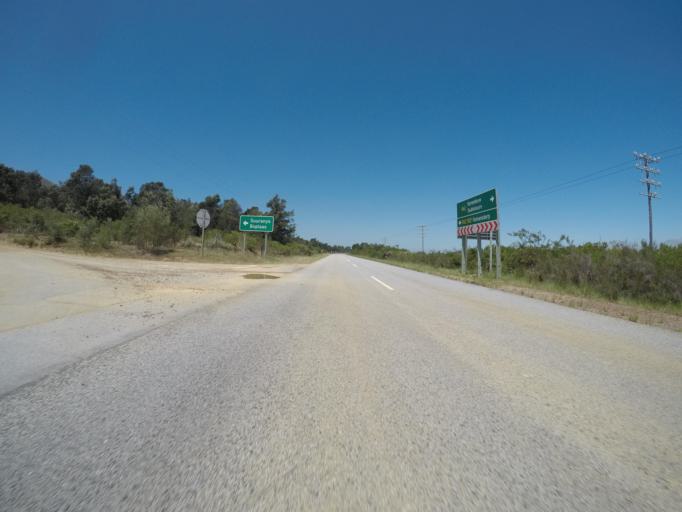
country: ZA
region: Eastern Cape
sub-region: Cacadu District Municipality
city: Kareedouw
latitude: -33.9606
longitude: 24.4215
